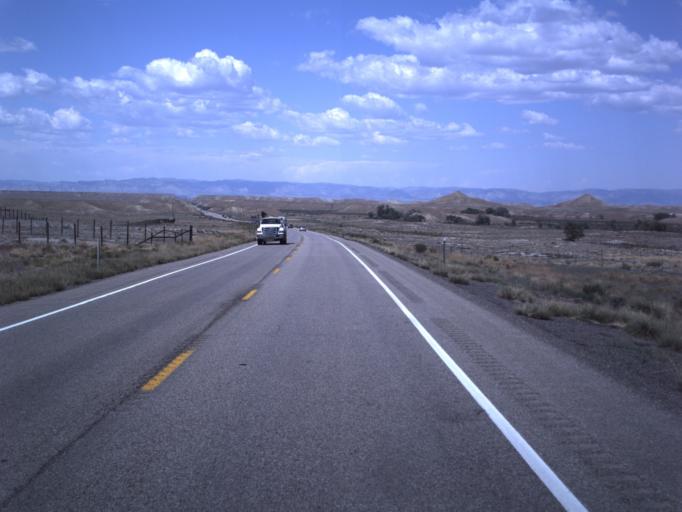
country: US
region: Utah
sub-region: Emery County
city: Huntington
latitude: 39.4212
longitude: -110.8718
